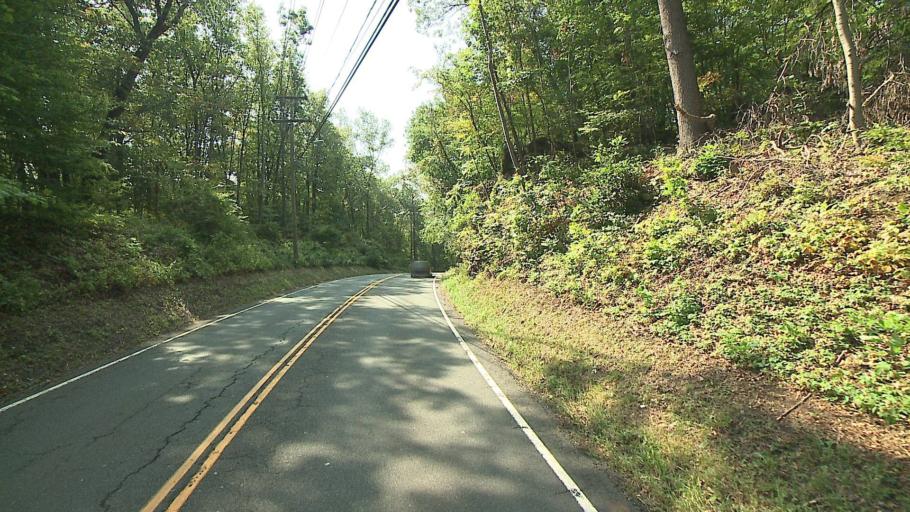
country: US
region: Connecticut
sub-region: Fairfield County
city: Ridgefield
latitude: 41.3170
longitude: -73.4787
